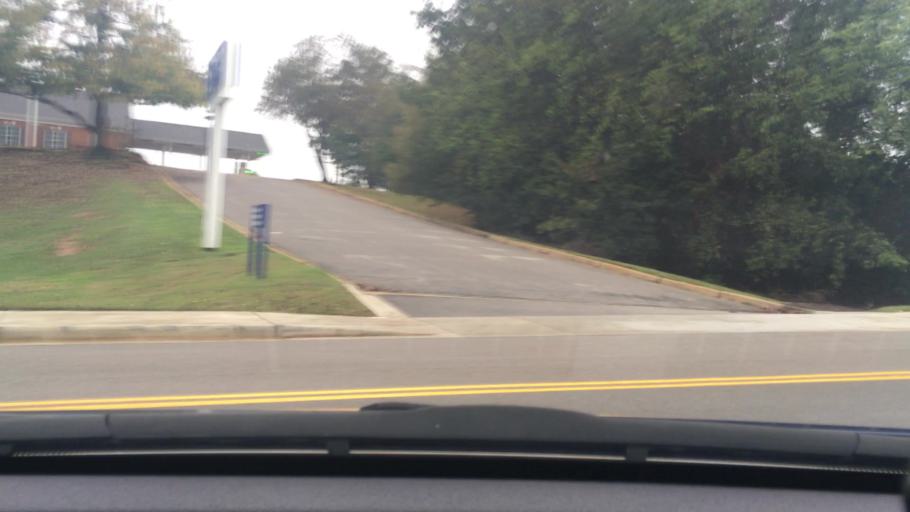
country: US
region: South Carolina
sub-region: Lexington County
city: Irmo
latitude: 34.0872
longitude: -81.1825
